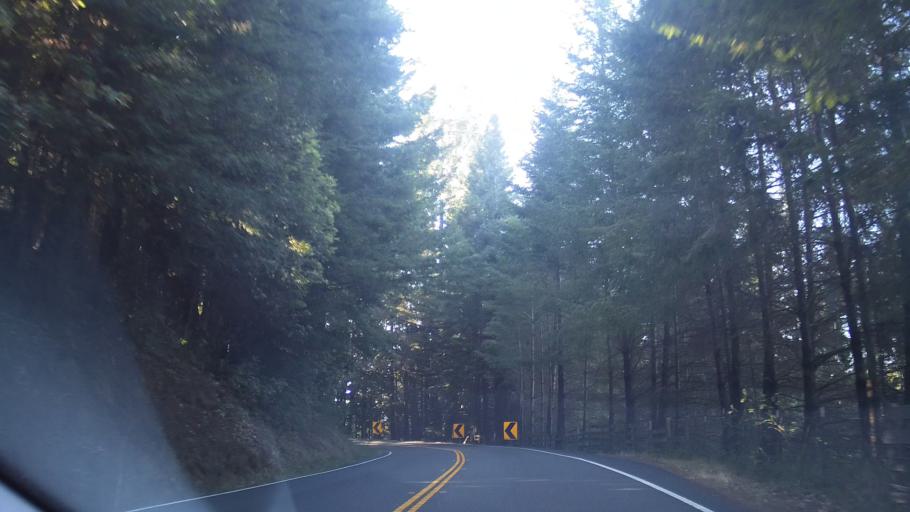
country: US
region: California
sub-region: Mendocino County
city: Fort Bragg
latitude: 39.3588
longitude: -123.6195
